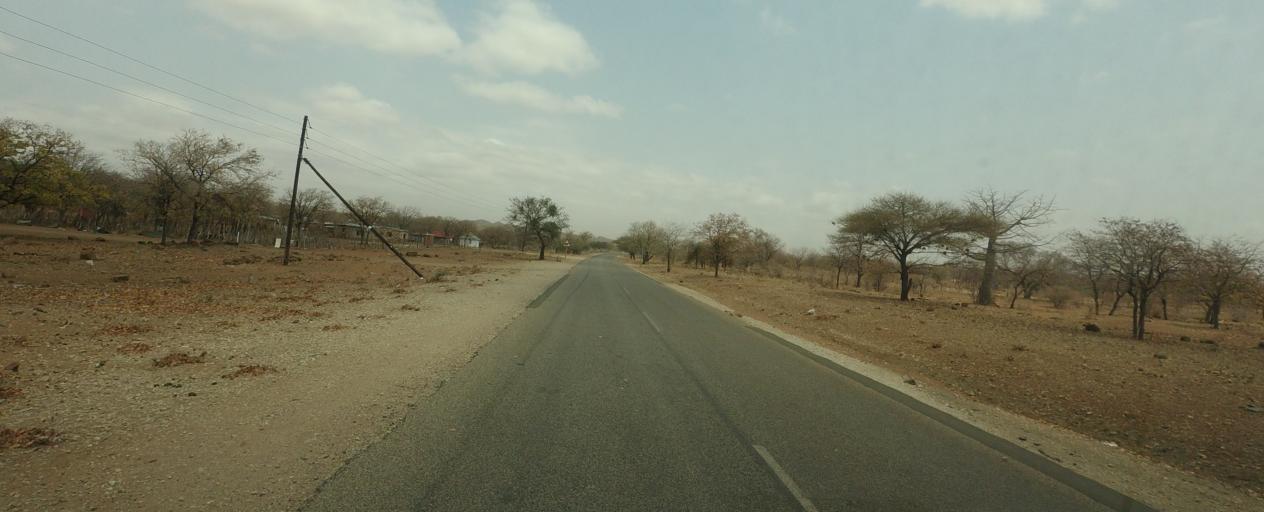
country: ZA
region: Limpopo
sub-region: Vhembe District Municipality
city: Mutale
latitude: -22.4230
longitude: 30.8897
